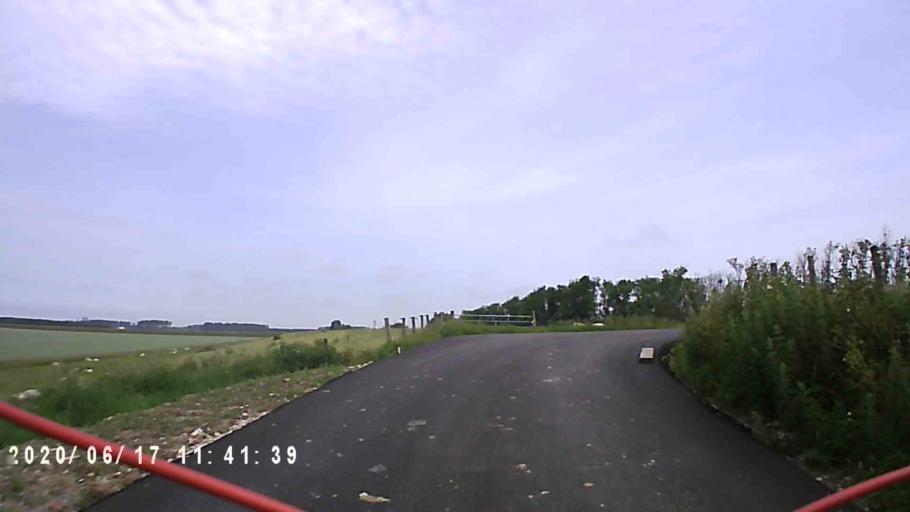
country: NL
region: Groningen
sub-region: Gemeente De Marne
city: Ulrum
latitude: 53.3616
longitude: 6.2791
